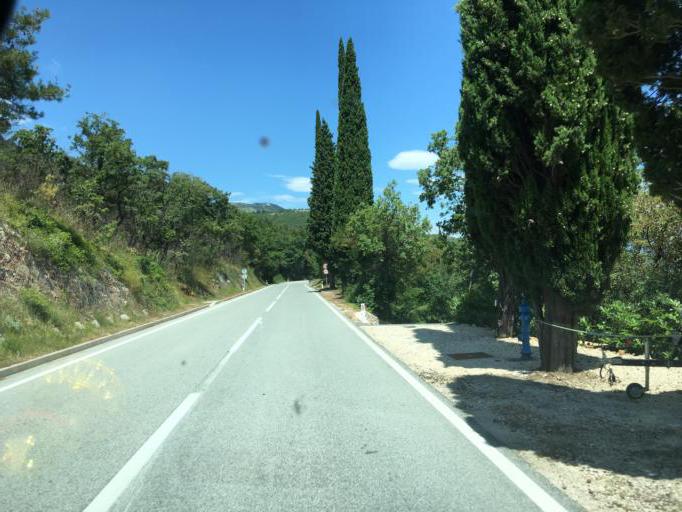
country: HR
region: Istarska
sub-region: Grad Labin
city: Rabac
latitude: 45.1299
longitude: 14.2045
